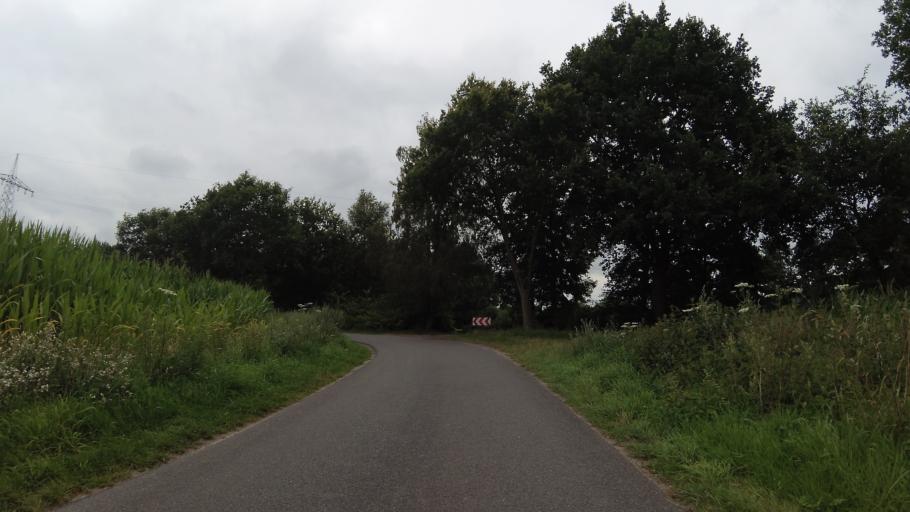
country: DE
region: Lower Saxony
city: Lathen
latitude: 52.8698
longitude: 7.3080
